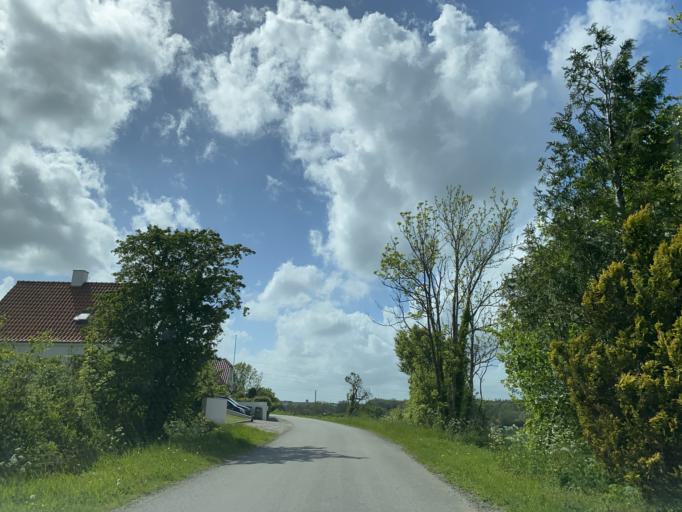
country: DK
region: South Denmark
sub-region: Aabenraa Kommune
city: Aabenraa
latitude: 55.0061
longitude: 9.4519
